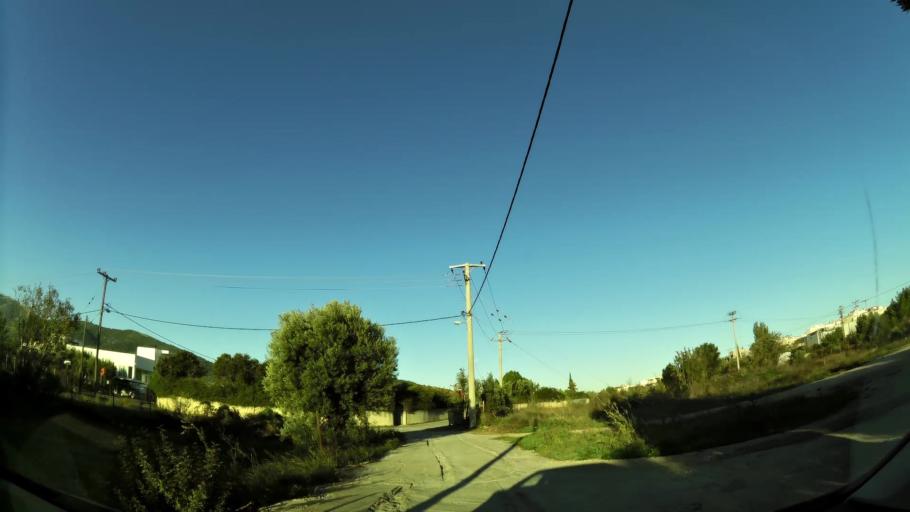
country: GR
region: Attica
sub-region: Nomarchia Anatolikis Attikis
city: Pallini
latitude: 38.0053
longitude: 23.8626
